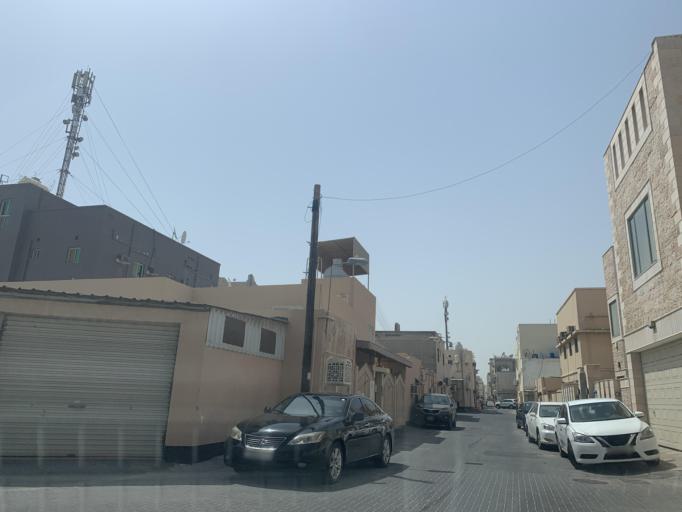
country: BH
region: Northern
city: Madinat `Isa
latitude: 26.1856
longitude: 50.5460
